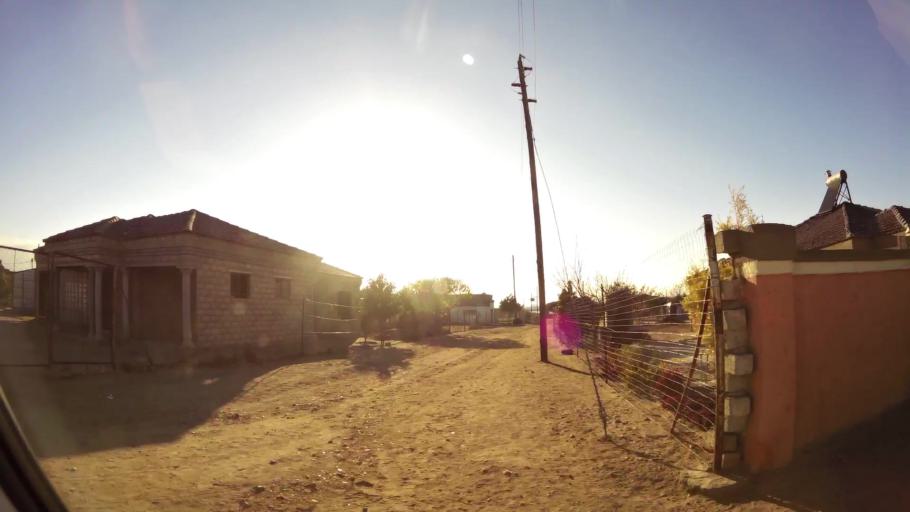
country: ZA
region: Limpopo
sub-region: Capricorn District Municipality
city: Polokwane
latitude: -23.8389
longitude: 29.3639
